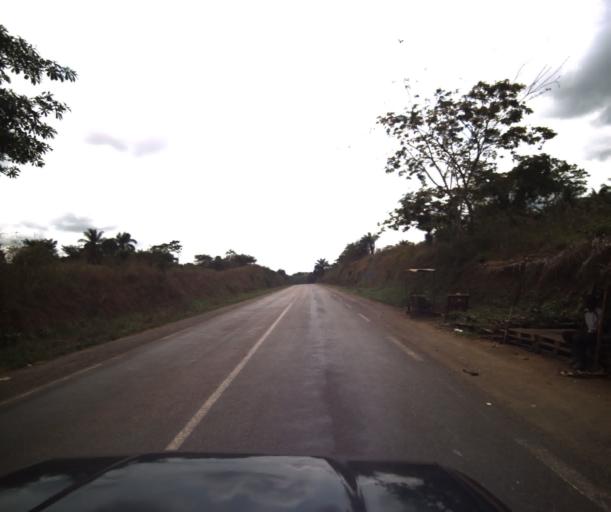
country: CM
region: Centre
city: Eseka
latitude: 3.8490
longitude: 10.5013
